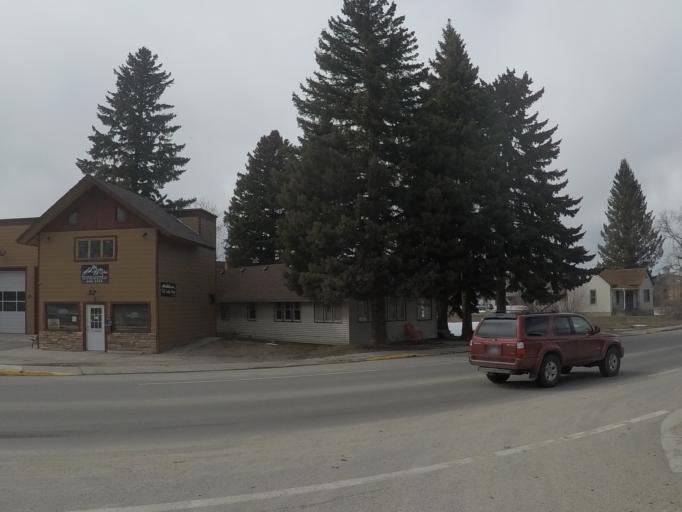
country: US
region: Montana
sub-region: Carbon County
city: Red Lodge
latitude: 45.1791
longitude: -109.2466
